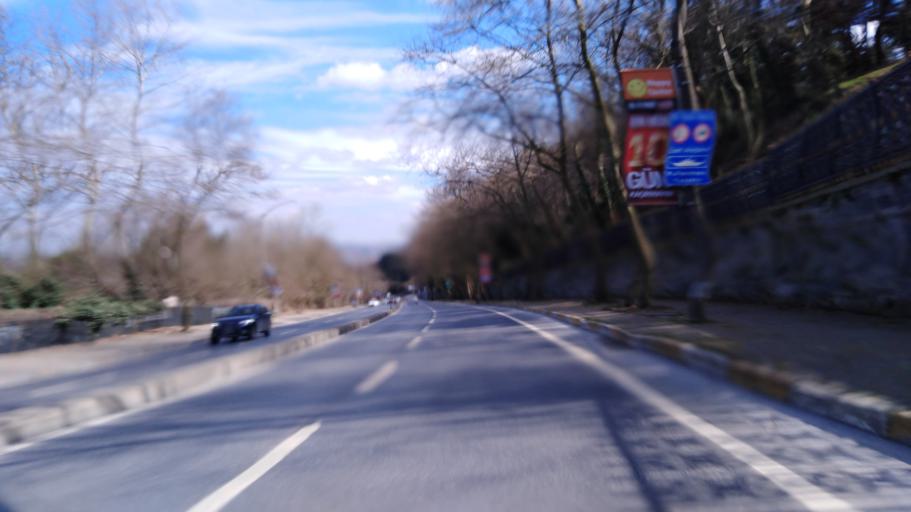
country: TR
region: Istanbul
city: Sisli
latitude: 41.1106
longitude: 29.0517
